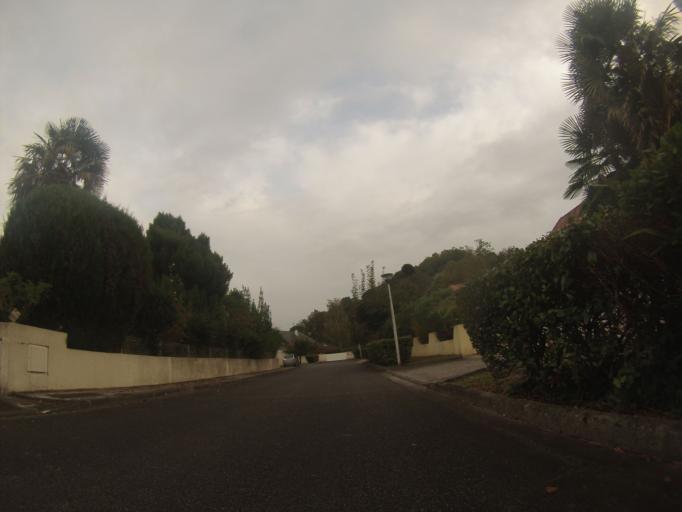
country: FR
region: Aquitaine
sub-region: Departement des Pyrenees-Atlantiques
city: Gelos
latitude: 43.2747
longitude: -0.3600
